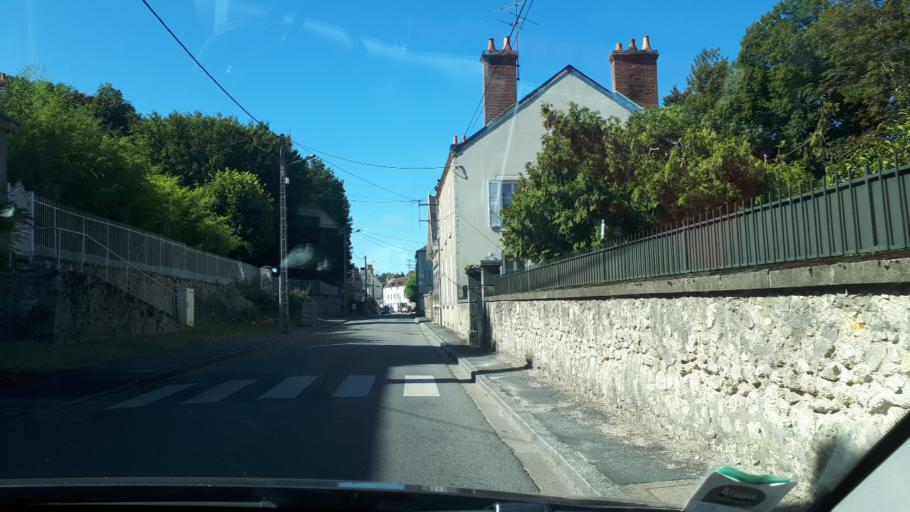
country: FR
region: Centre
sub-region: Departement du Loiret
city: Briare
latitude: 47.5936
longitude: 2.7555
